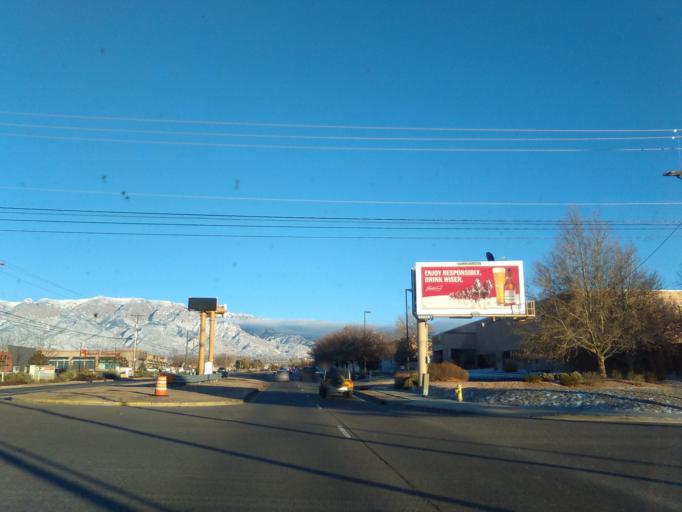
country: US
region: New Mexico
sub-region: Bernalillo County
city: North Valley
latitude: 35.1845
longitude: -106.5955
